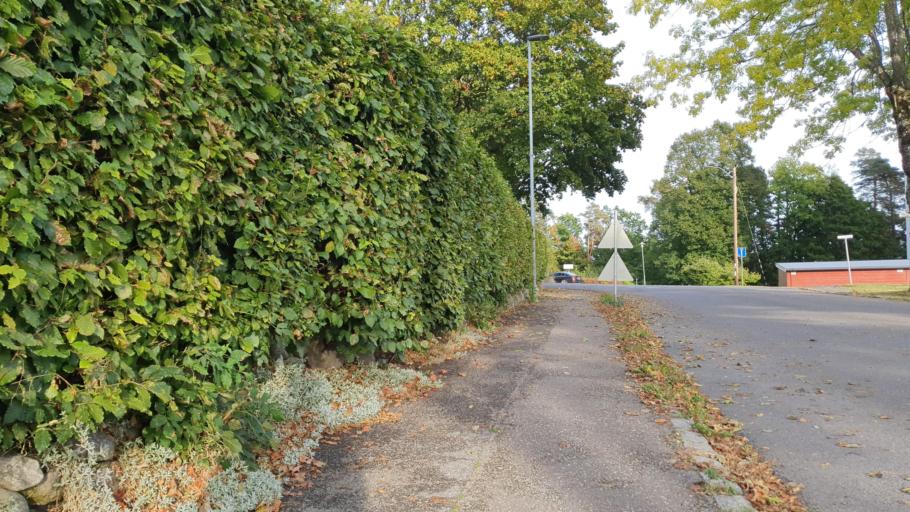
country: NO
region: Vestfold
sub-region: Tonsberg
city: Tonsberg
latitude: 59.2797
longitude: 10.4255
